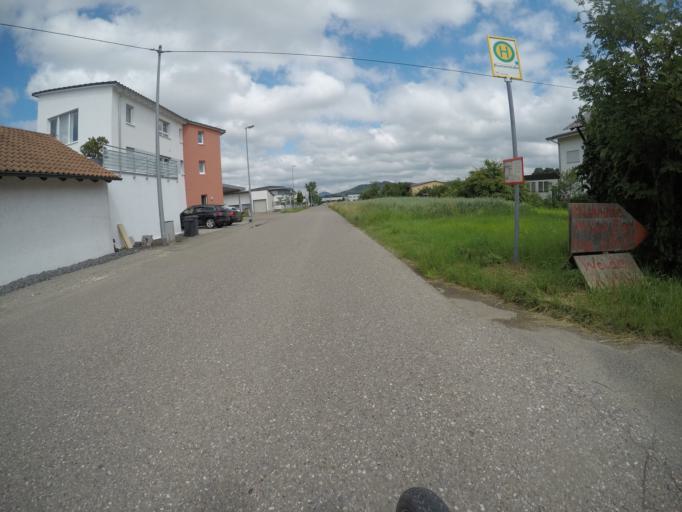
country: DE
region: Baden-Wuerttemberg
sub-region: Regierungsbezirk Stuttgart
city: Gingen an der Fils
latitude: 48.6646
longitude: 9.7797
